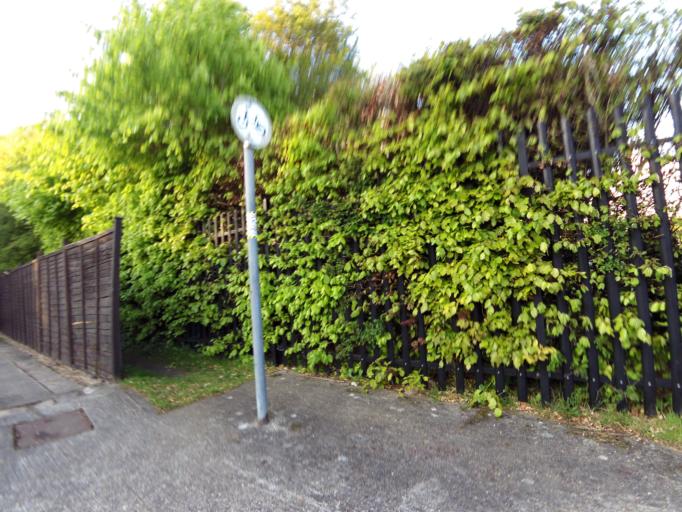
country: GB
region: England
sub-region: Suffolk
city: Ipswich
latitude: 52.0720
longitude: 1.1775
